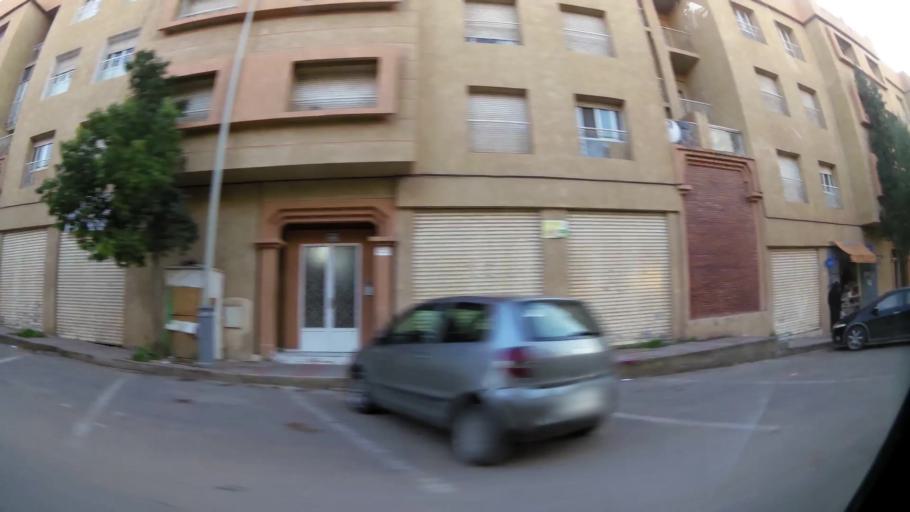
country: MA
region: Chaouia-Ouardigha
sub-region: Settat Province
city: Settat
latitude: 32.9886
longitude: -7.6100
